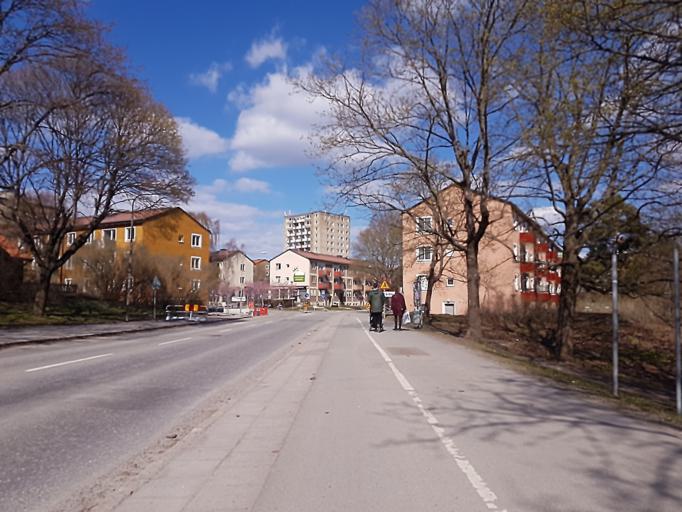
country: SE
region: Stockholm
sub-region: Nacka Kommun
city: Nacka
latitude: 59.2823
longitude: 18.1130
